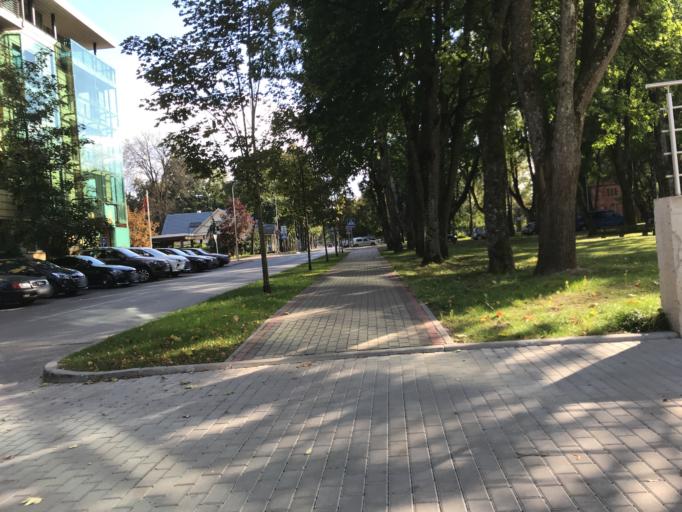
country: LT
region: Alytaus apskritis
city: Druskininkai
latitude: 54.0185
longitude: 23.9758
